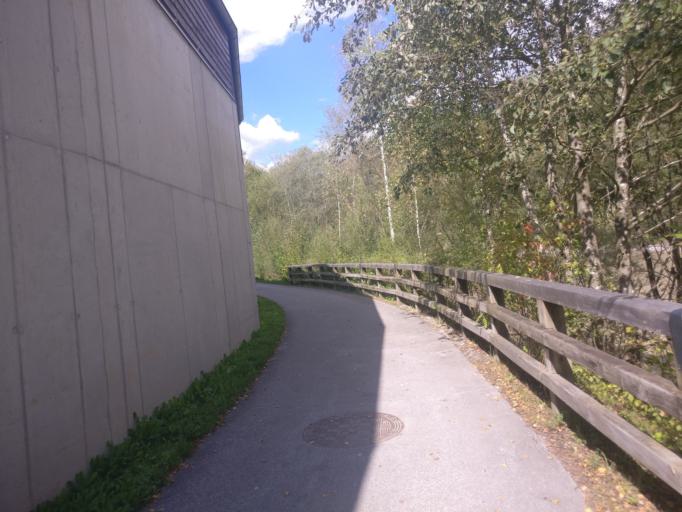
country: AT
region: Salzburg
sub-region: Politischer Bezirk Sankt Johann im Pongau
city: Bischofshofen
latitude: 47.4225
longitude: 13.2240
